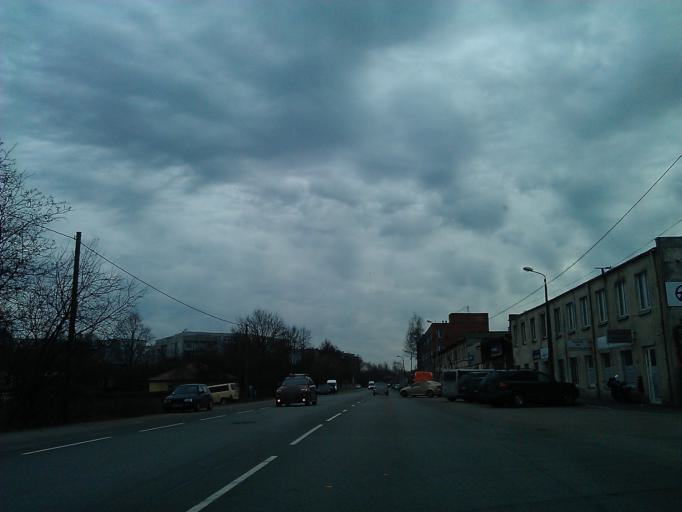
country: LV
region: Riga
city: Riga
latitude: 56.9600
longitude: 24.1653
